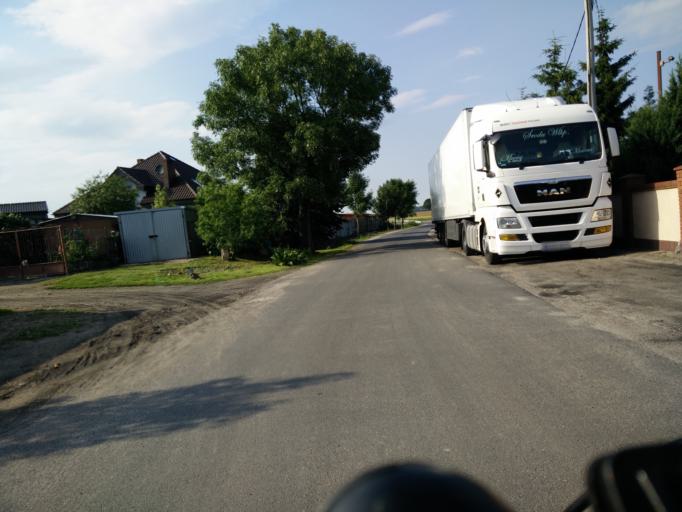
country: PL
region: Greater Poland Voivodeship
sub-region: Powiat sredzki
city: Sroda Wielkopolska
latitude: 52.2648
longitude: 17.3117
